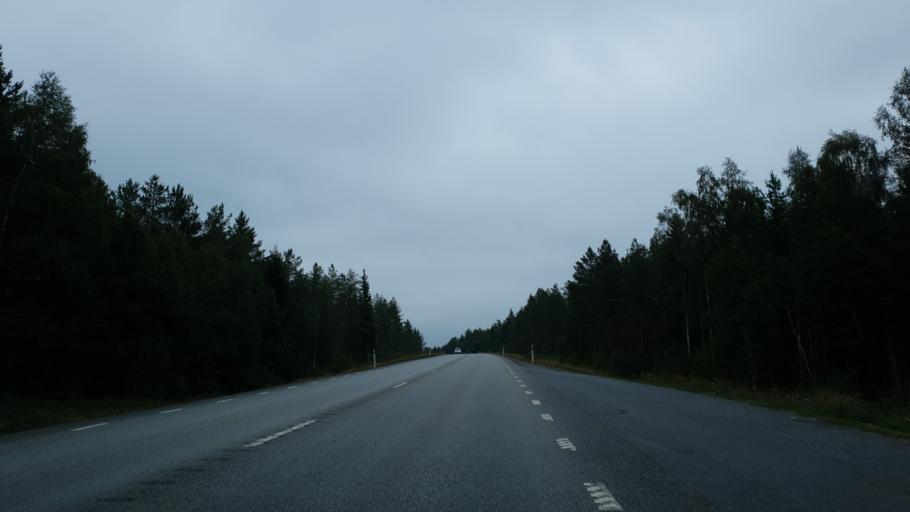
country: SE
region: Vaesterbotten
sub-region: Robertsfors Kommun
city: Robertsfors
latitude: 64.2771
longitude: 21.0580
